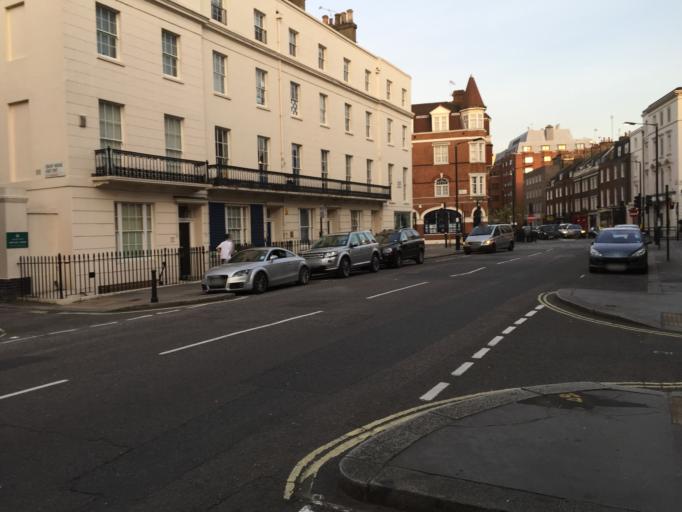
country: GB
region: England
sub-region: Greater London
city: Battersea
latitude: 51.4951
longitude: -0.1491
